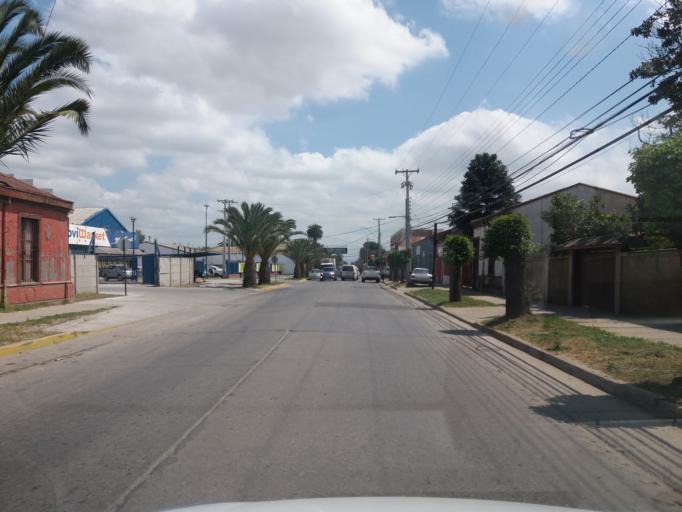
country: CL
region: Valparaiso
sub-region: Provincia de Marga Marga
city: Limache
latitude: -33.0065
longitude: -71.2550
